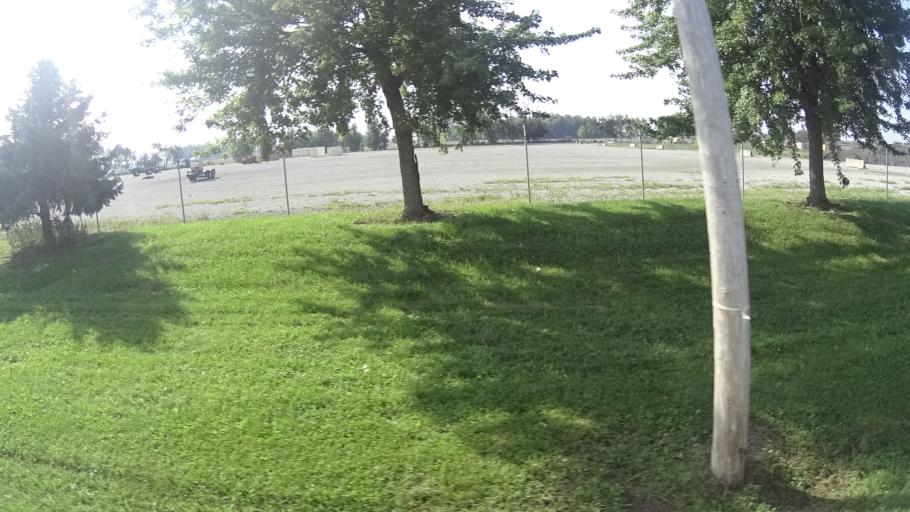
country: US
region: Indiana
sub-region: Madison County
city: Lapel
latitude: 40.0096
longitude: -85.8510
